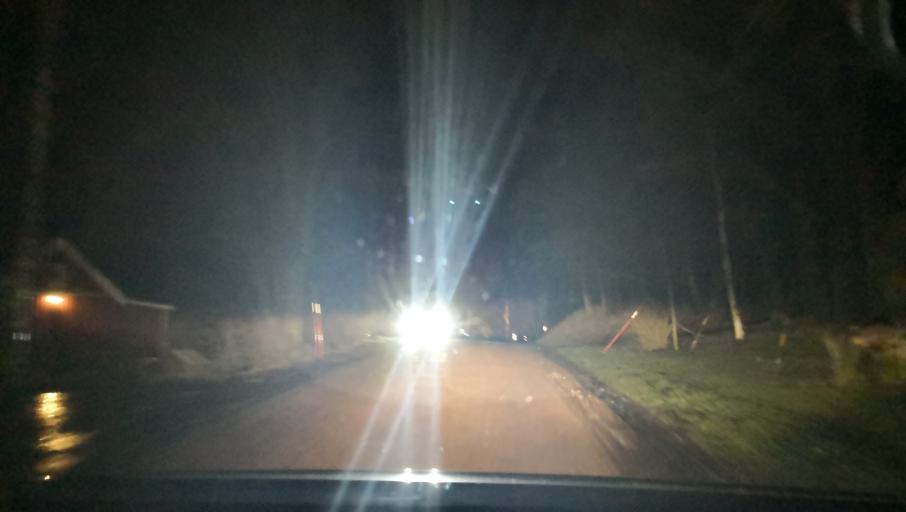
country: SE
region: Vaestmanland
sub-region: Vasteras
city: Tillberga
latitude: 59.6815
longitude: 16.7007
